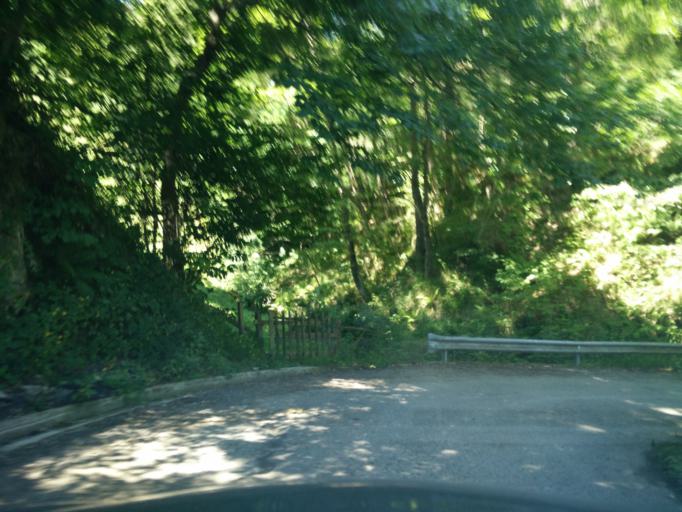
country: ES
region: Asturias
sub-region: Province of Asturias
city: Amieva
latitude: 43.1988
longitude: -5.1273
